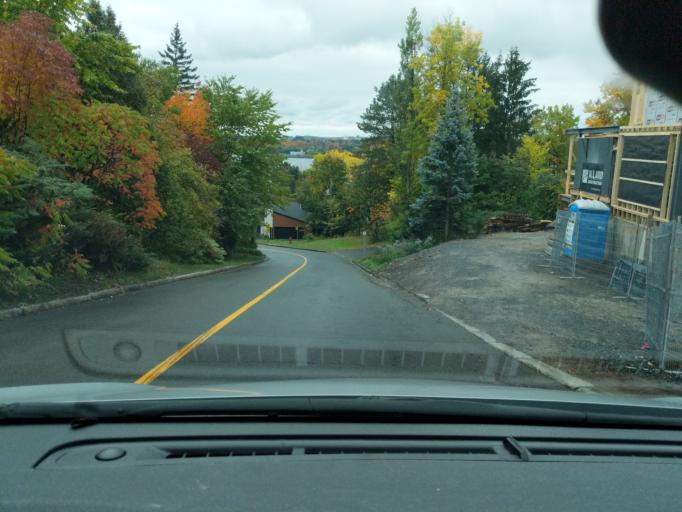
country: CA
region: Quebec
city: Quebec
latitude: 46.7639
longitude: -71.2680
